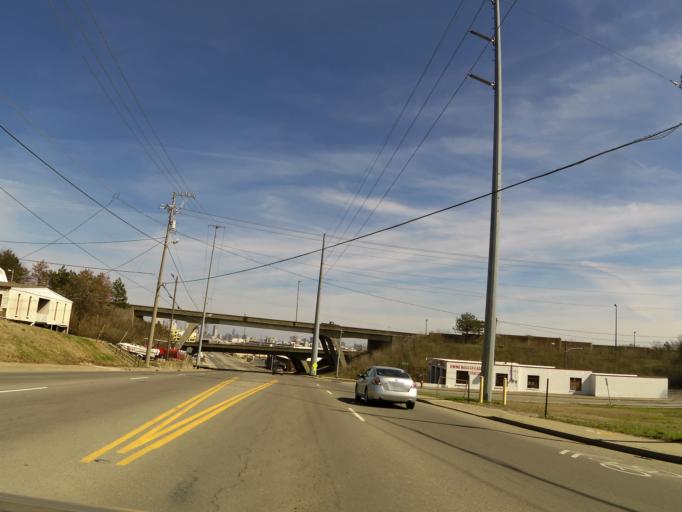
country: US
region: Tennessee
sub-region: Davidson County
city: Nashville
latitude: 36.1529
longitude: -86.8242
